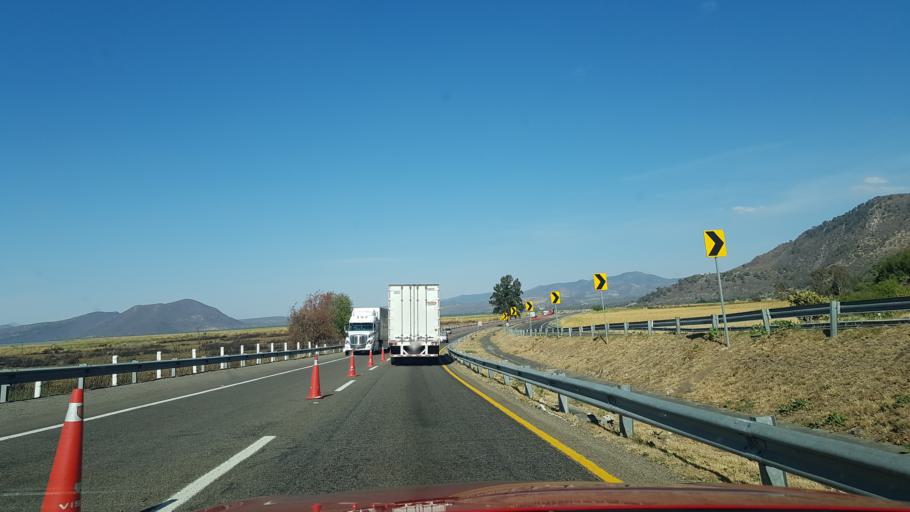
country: MX
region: Michoacan
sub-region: Zinapecuaro
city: Jose Maria Morelos (La Yegueeria)
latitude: 19.8969
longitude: -100.8956
